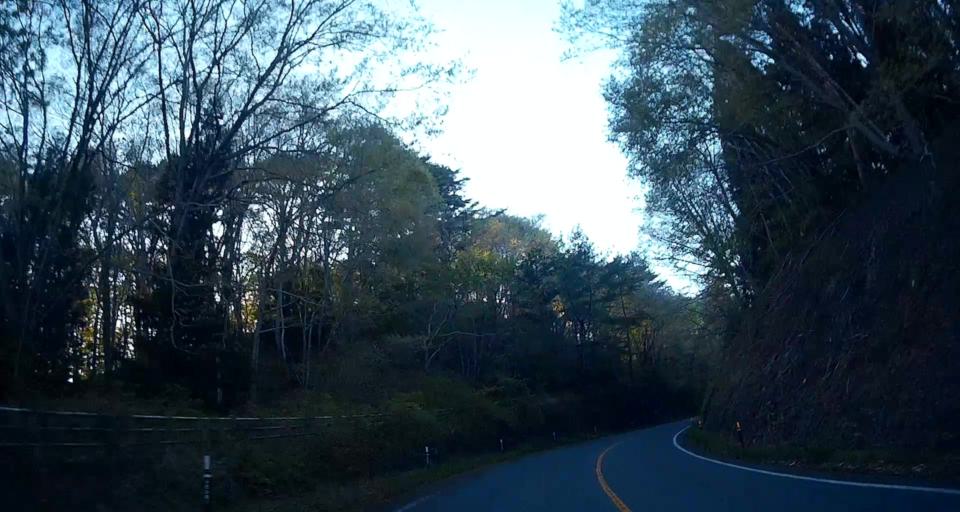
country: JP
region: Iwate
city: Miyako
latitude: 39.6526
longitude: 141.9671
